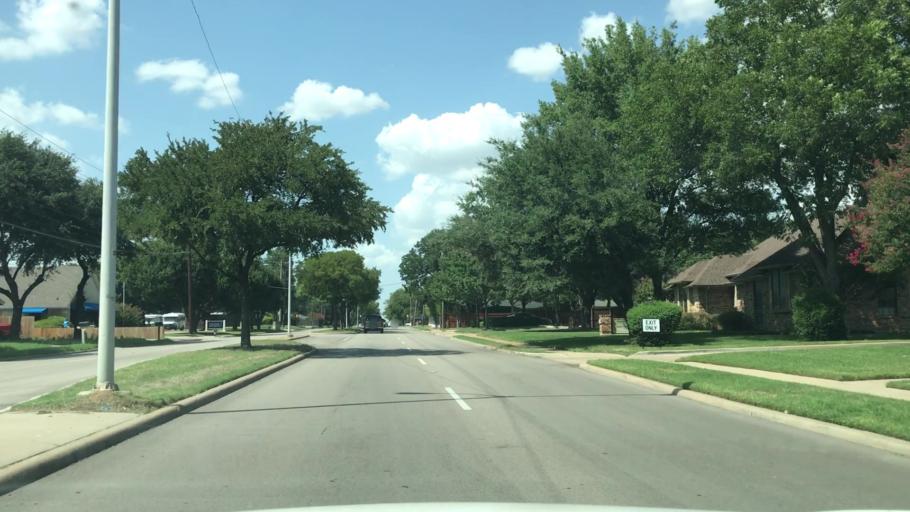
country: US
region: Texas
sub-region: Dallas County
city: Irving
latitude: 32.8472
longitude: -96.9504
